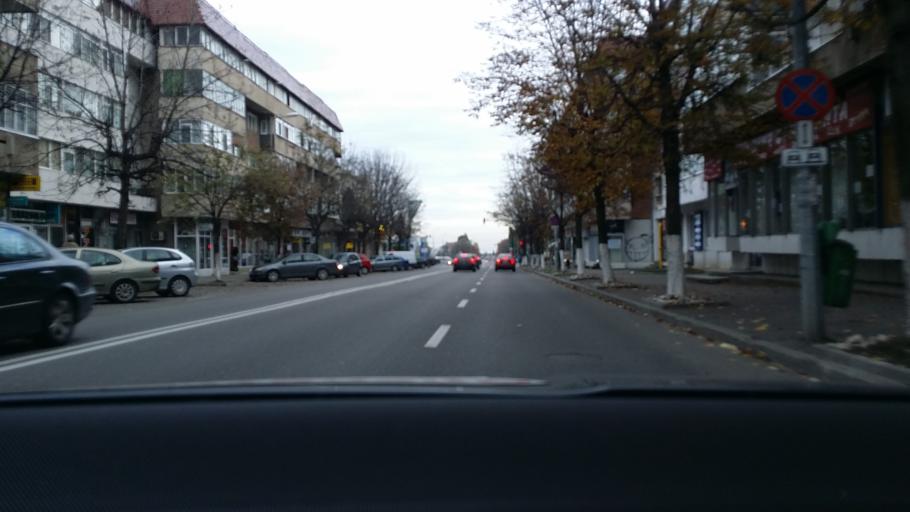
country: RO
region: Prahova
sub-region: Municipiul Campina
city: Campina
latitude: 45.1211
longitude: 25.7378
